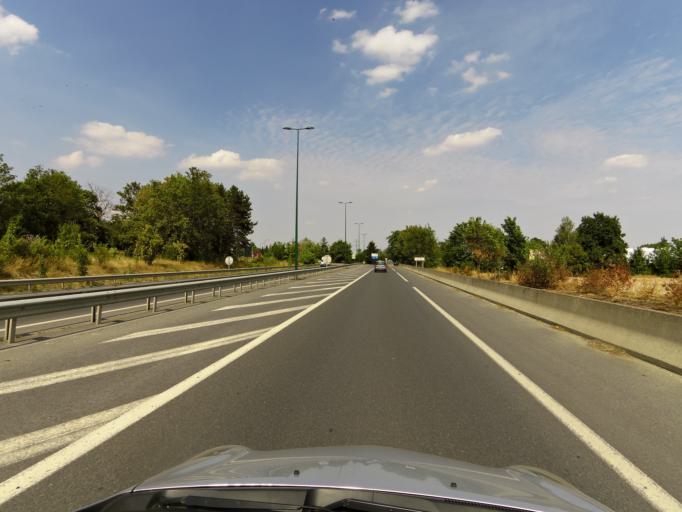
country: FR
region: Champagne-Ardenne
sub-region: Departement de la Marne
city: Bezannes
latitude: 49.2113
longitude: 4.0142
